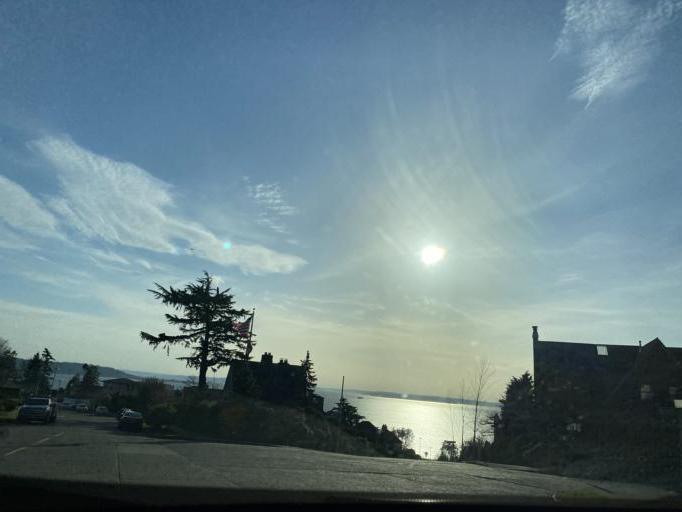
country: US
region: Washington
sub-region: King County
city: Seattle
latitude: 47.6395
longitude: -122.4062
